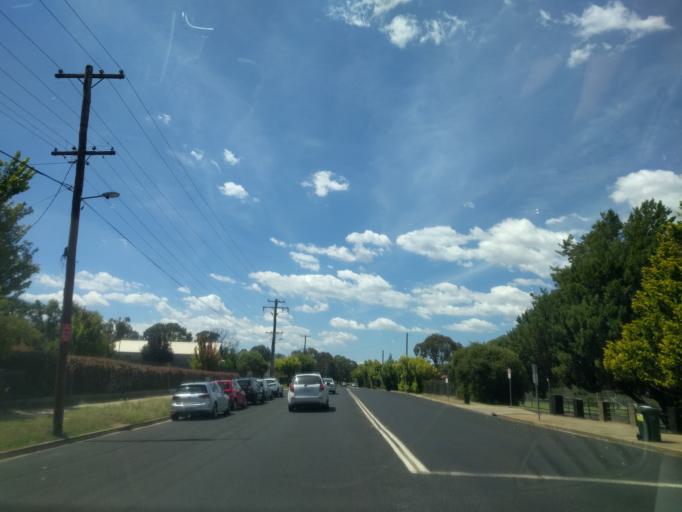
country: AU
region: New South Wales
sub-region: Armidale Dumaresq
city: Armidale
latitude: -30.5024
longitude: 151.6735
